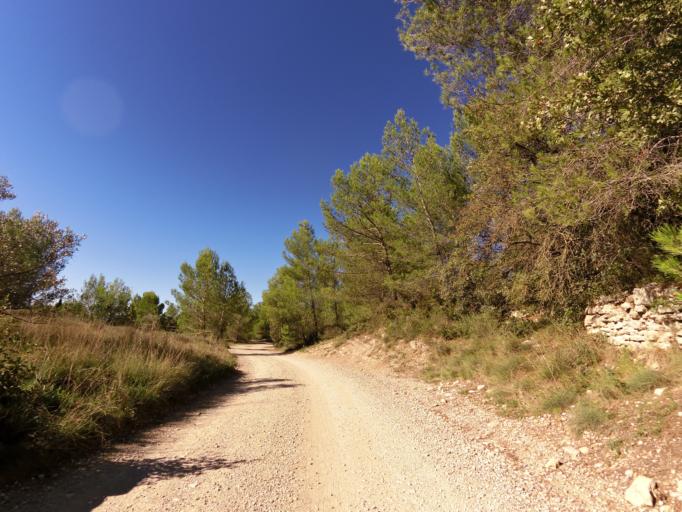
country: FR
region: Languedoc-Roussillon
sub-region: Departement du Gard
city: Aubais
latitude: 43.7427
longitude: 4.1518
